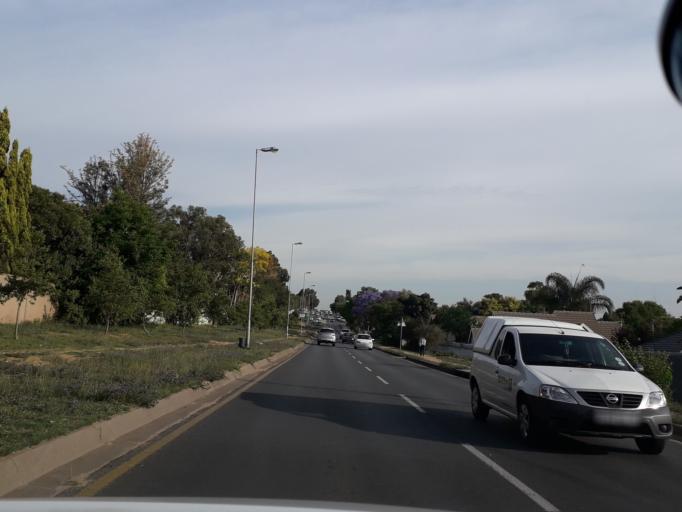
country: ZA
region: Gauteng
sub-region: City of Johannesburg Metropolitan Municipality
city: Diepsloot
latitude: -26.0355
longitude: 27.9929
